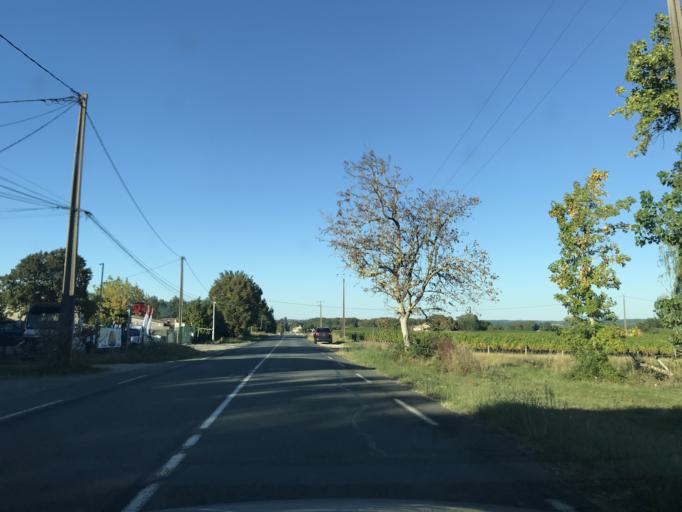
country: FR
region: Aquitaine
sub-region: Departement de la Gironde
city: Sauveterre-de-Guyenne
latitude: 44.6455
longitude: -0.1263
